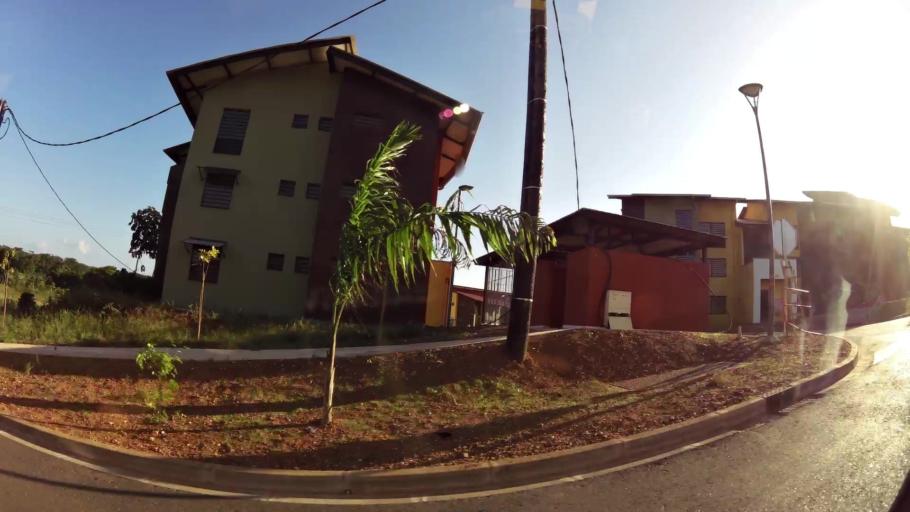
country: GF
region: Guyane
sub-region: Guyane
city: Remire-Montjoly
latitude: 4.8858
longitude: -52.2969
